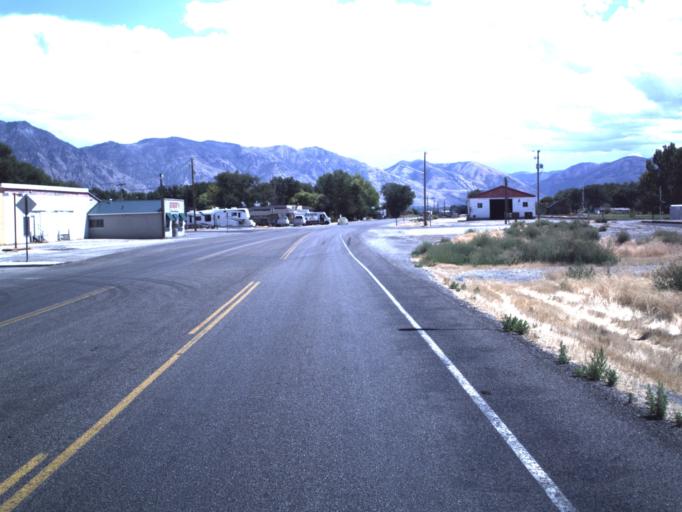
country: US
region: Utah
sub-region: Box Elder County
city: Honeyville
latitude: 41.5514
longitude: -112.1122
